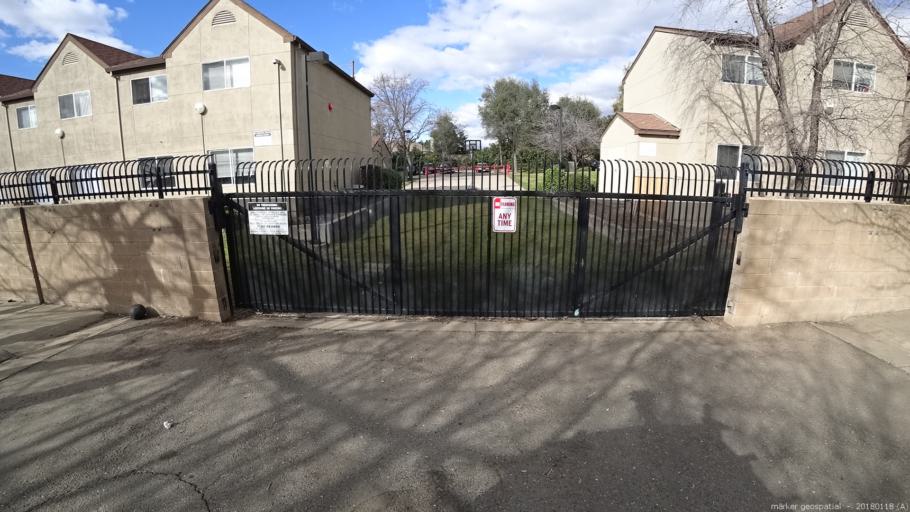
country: US
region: California
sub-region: Sacramento County
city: Orangevale
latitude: 38.6835
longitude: -121.2037
